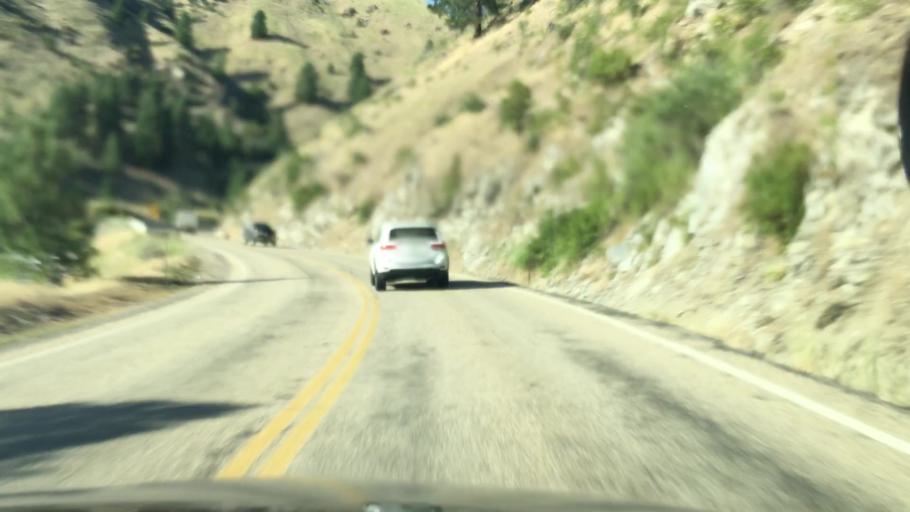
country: US
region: Idaho
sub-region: Boise County
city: Idaho City
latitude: 44.0878
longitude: -116.1118
